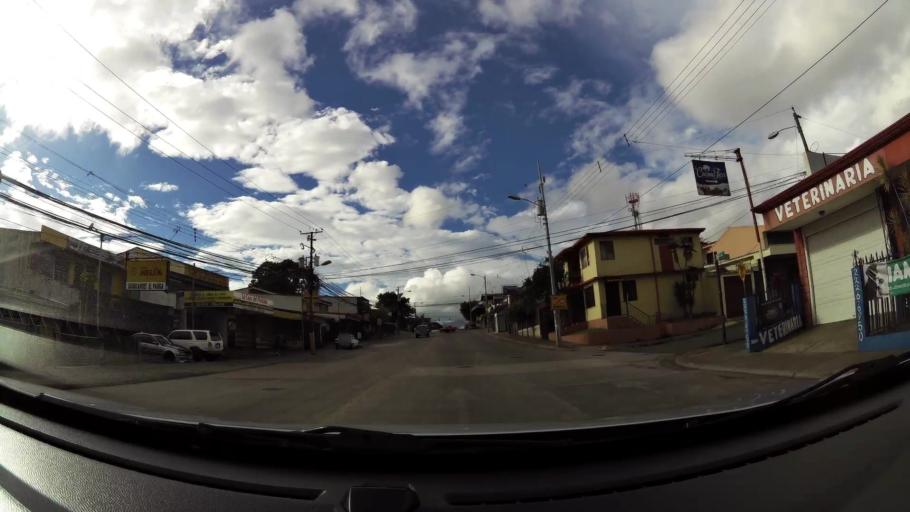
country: CR
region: San Jose
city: San Pedro
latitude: 9.9130
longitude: -84.0569
